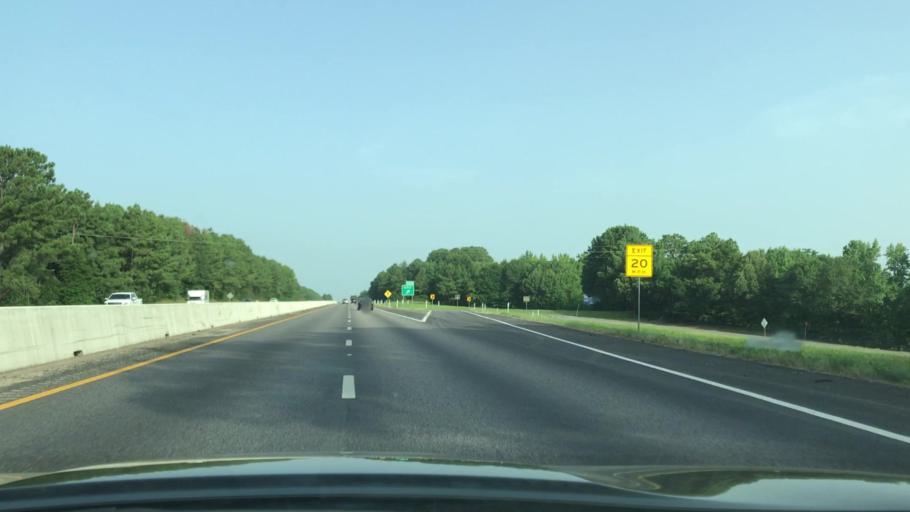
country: US
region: Texas
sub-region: Smith County
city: Tyler
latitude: 32.4585
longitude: -95.3113
